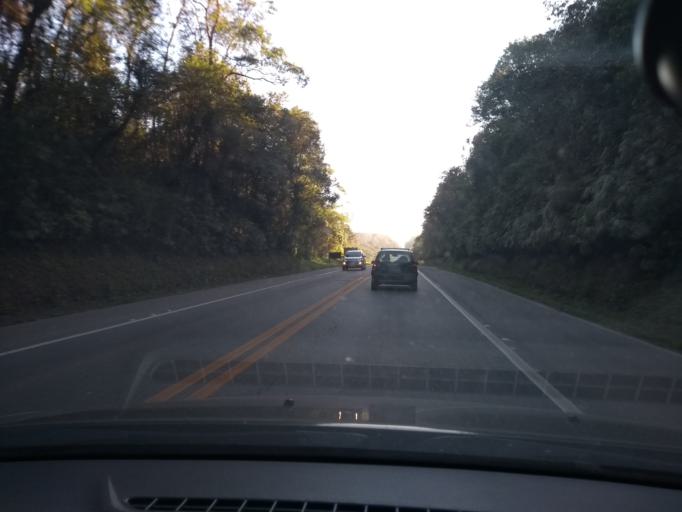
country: BR
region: Sao Paulo
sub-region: Rio Grande Da Serra
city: Rio Grande da Serra
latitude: -23.7752
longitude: -46.4797
